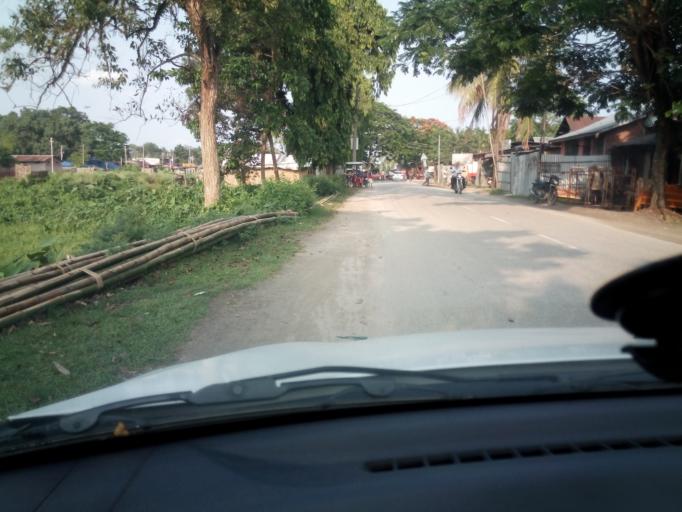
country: IN
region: Assam
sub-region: Udalguri
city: Udalguri
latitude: 26.7439
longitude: 92.0939
